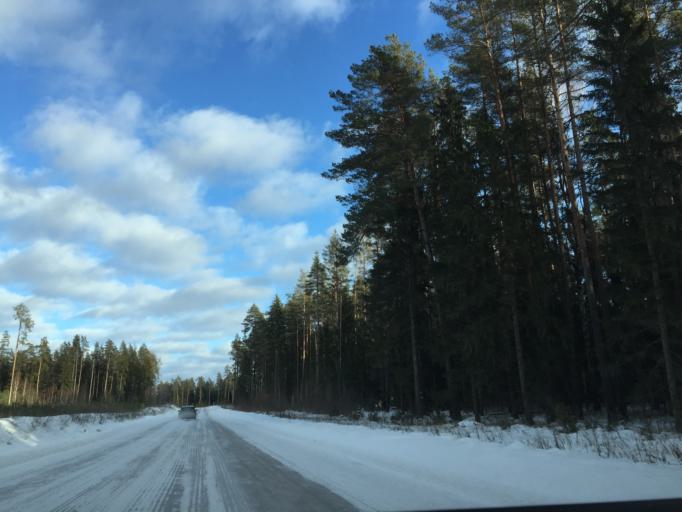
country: LV
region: Ogre
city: Jumprava
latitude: 56.5887
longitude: 24.9723
